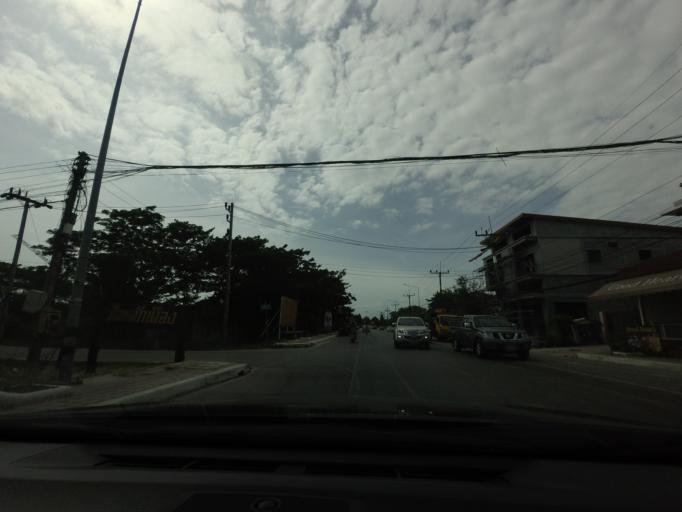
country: TH
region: Pattani
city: Pattani
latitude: 6.8812
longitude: 101.2460
